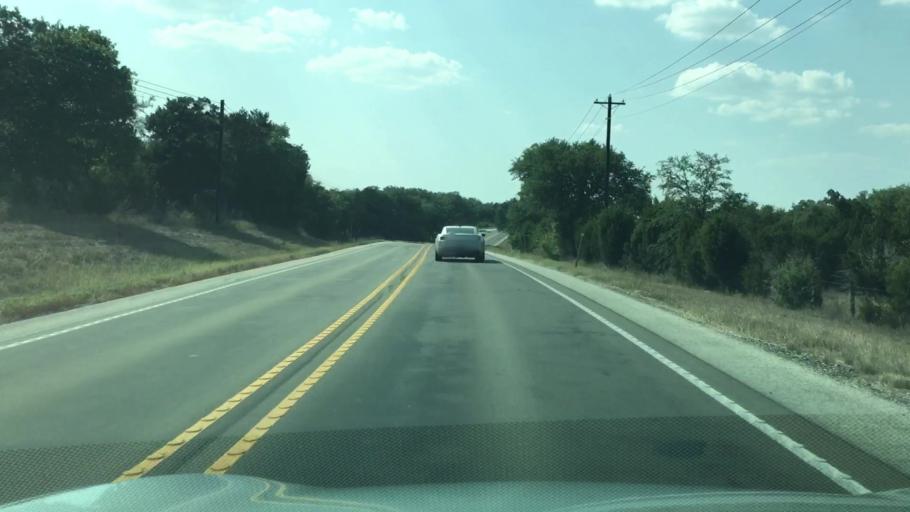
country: US
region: Texas
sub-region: Hays County
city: Woodcreek
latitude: 30.0771
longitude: -98.0949
